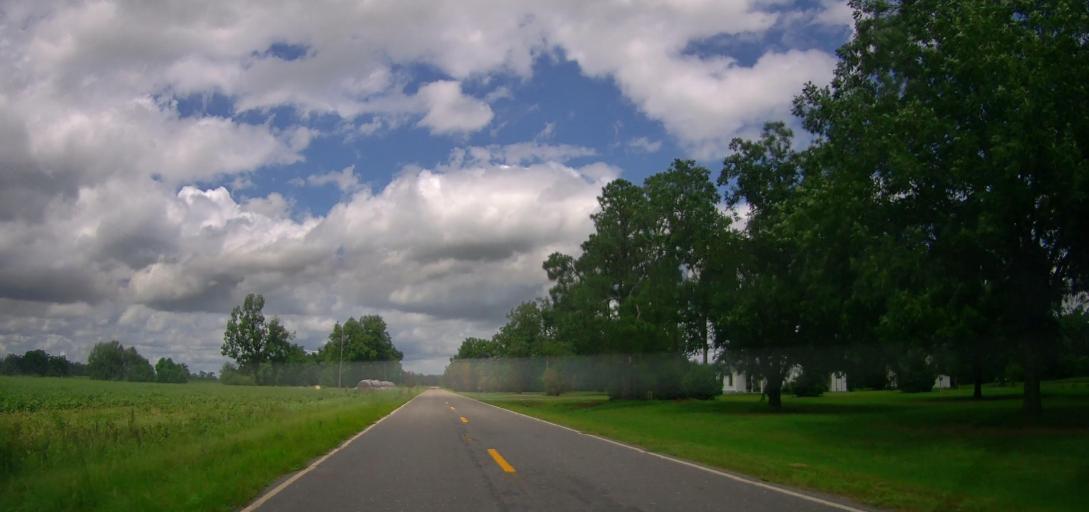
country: US
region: Georgia
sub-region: Ben Hill County
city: Fitzgerald
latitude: 31.6539
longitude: -83.4012
